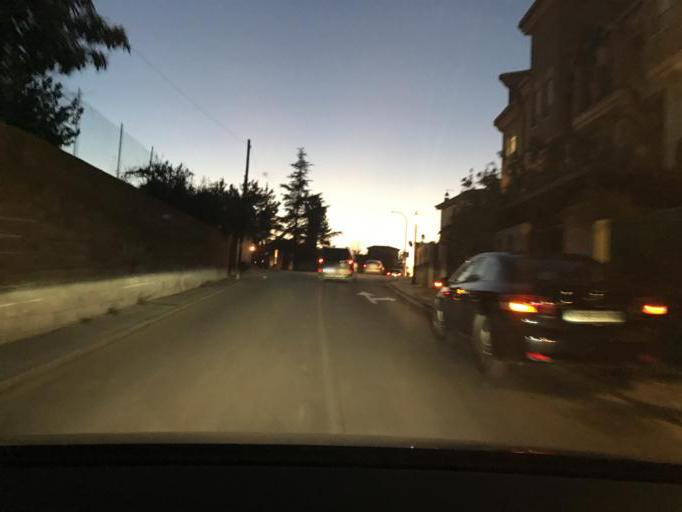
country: ES
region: Andalusia
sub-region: Provincia de Granada
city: Ogijares
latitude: 37.1132
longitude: -3.6164
